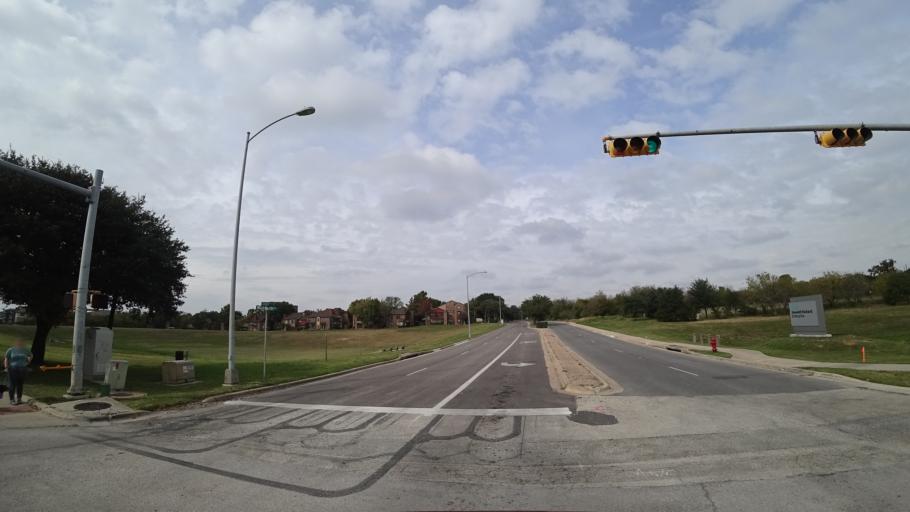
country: US
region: Texas
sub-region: Travis County
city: Wells Branch
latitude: 30.4416
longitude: -97.6921
